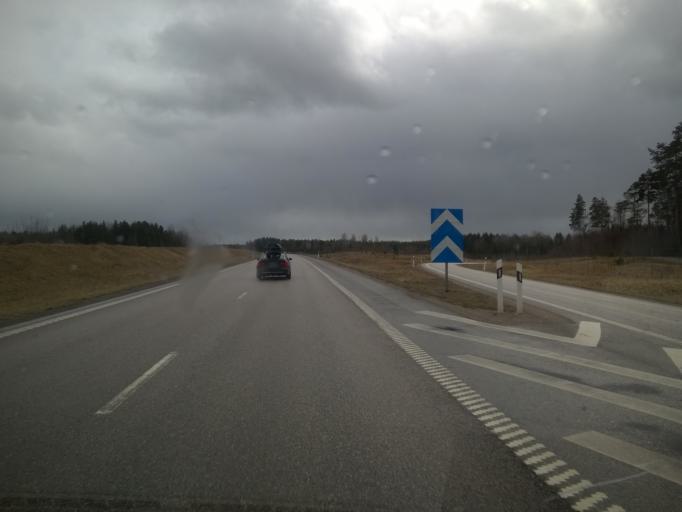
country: SE
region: Uppsala
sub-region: Osthammars Kommun
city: Bjorklinge
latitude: 60.0144
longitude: 17.6237
